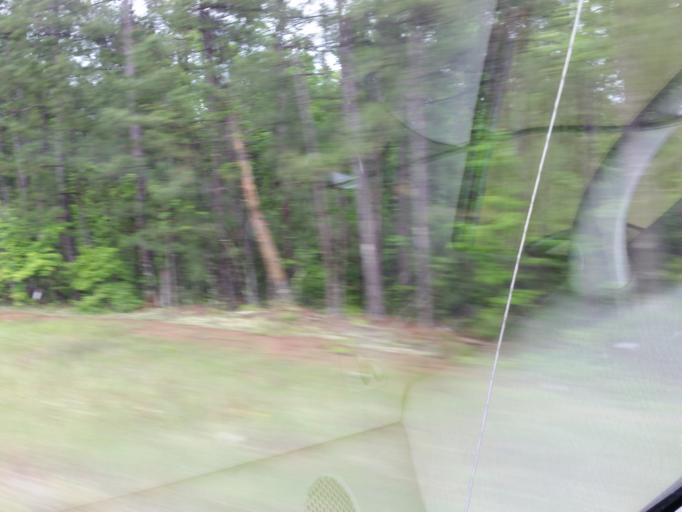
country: US
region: Georgia
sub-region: Peach County
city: Fort Valley
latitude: 32.6699
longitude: -83.8813
